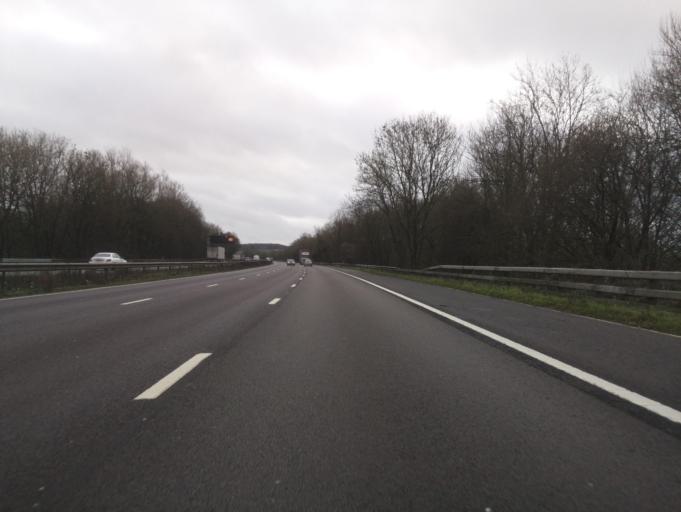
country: GB
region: England
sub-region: Staffordshire
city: Audley
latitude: 53.0082
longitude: -2.3294
